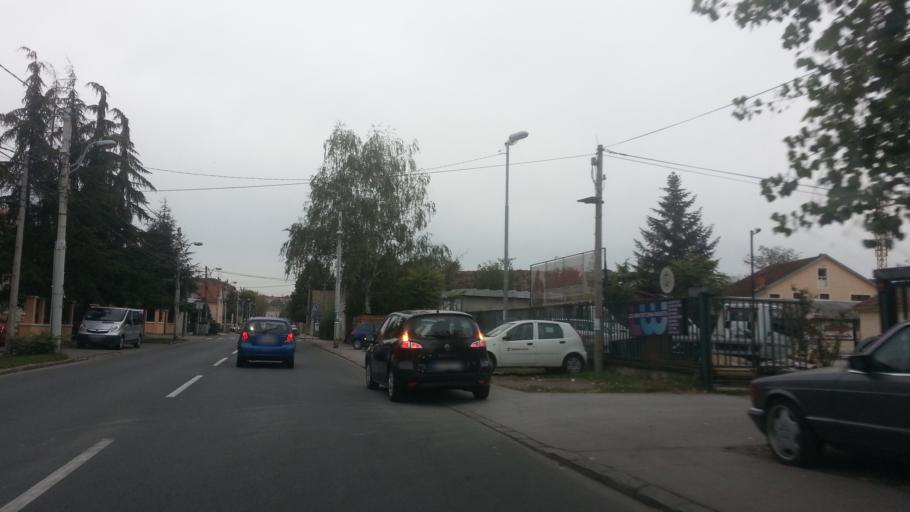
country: RS
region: Central Serbia
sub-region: Belgrade
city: Zemun
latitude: 44.8369
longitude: 20.4023
